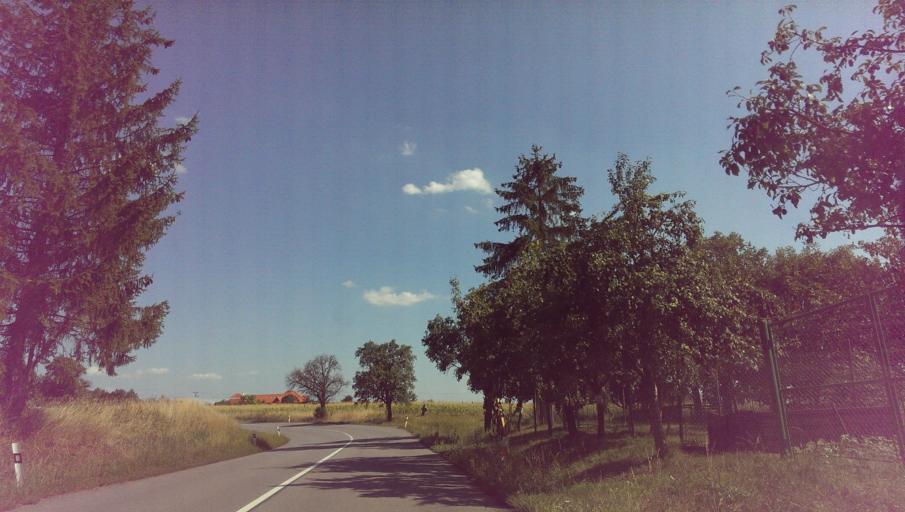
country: CZ
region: Zlin
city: Holesov
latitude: 49.3080
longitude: 17.6070
